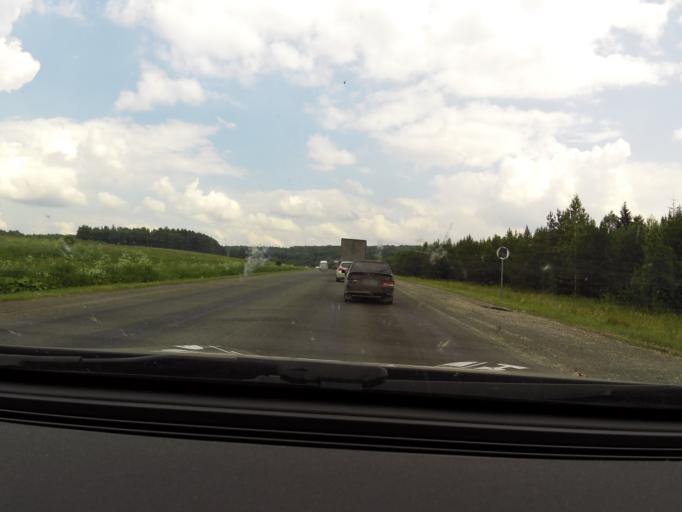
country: RU
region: Sverdlovsk
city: Ufimskiy
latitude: 56.7824
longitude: 58.2787
